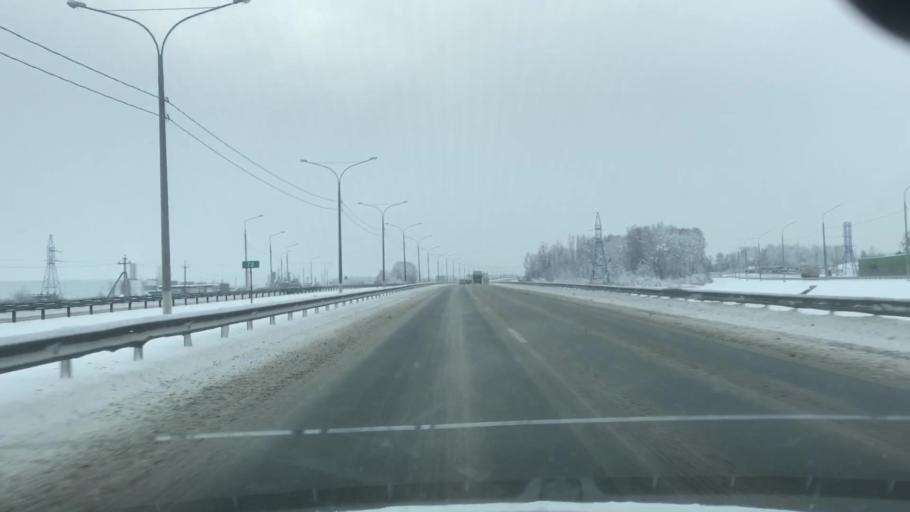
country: RU
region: Moskovskaya
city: Mikhnevo
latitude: 55.1562
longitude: 37.9285
